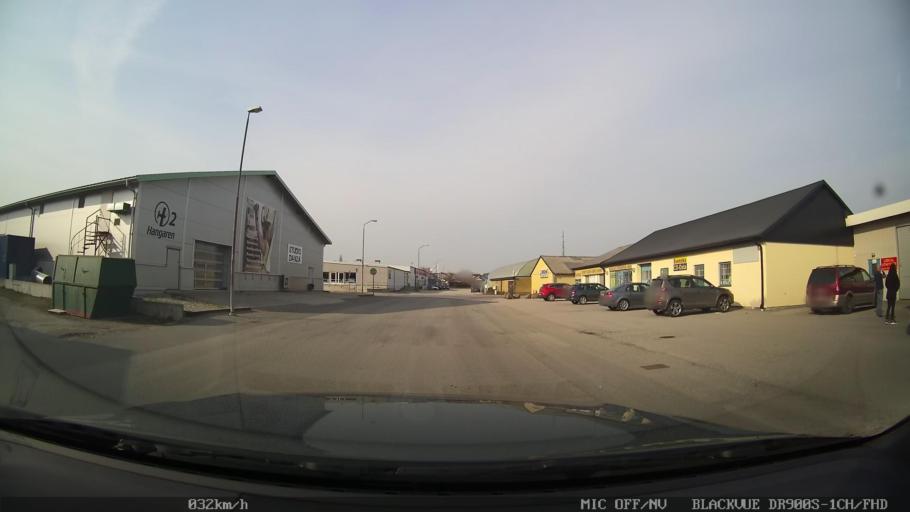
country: SE
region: Skane
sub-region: Ystads Kommun
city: Ystad
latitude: 55.4392
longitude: 13.8367
